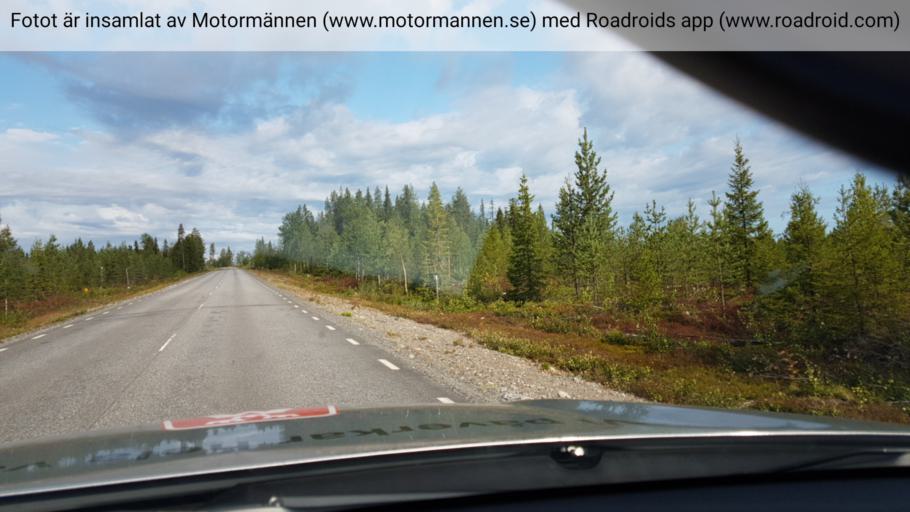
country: SE
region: Vaesterbotten
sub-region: Skelleftea Kommun
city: Storvik
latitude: 65.3469
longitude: 20.5056
